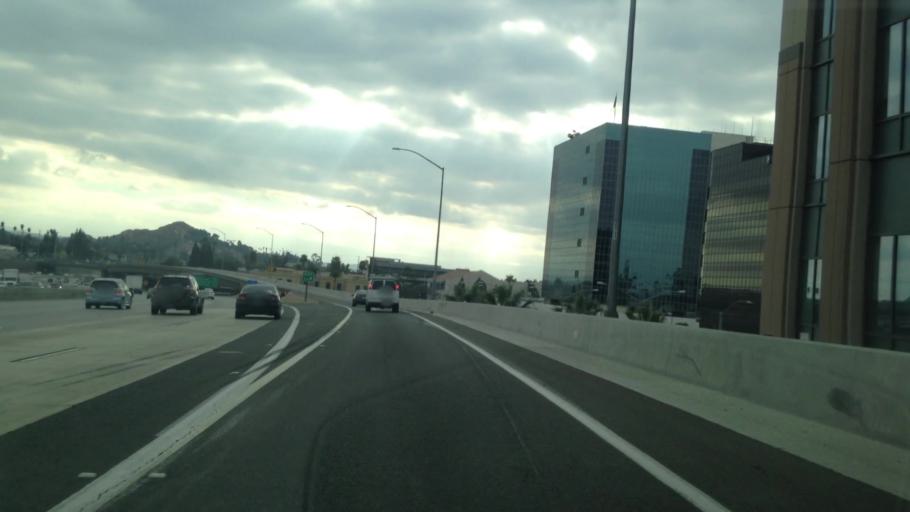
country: US
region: California
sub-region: Riverside County
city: Riverside
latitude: 33.9795
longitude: -117.3708
